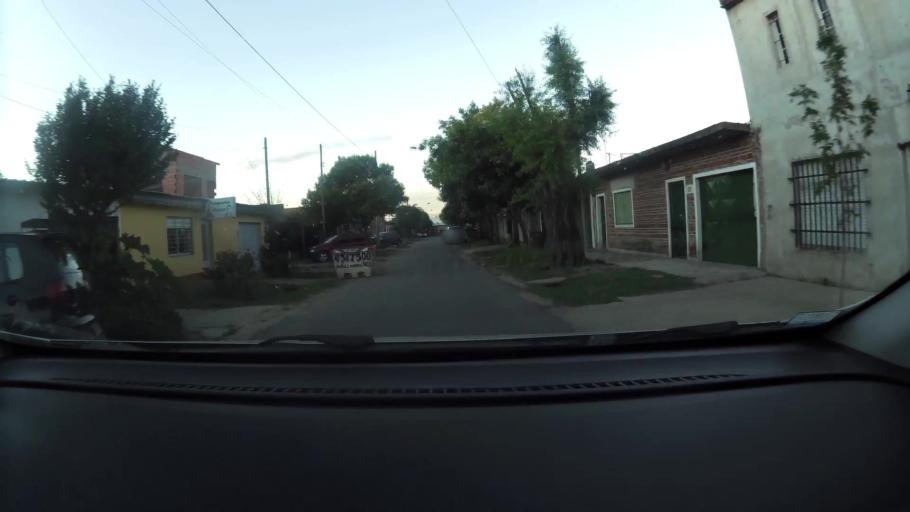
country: AR
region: Santa Fe
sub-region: Departamento de Rosario
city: Rosario
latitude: -32.9691
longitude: -60.6874
